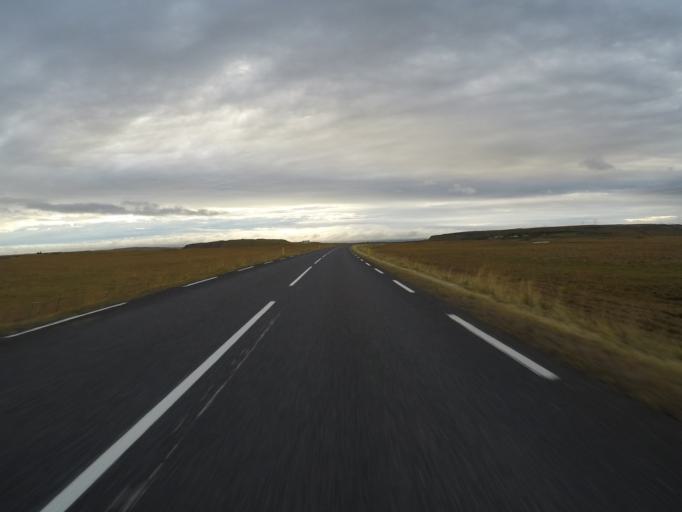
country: IS
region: South
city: Vestmannaeyjar
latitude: 64.0451
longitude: -20.1648
